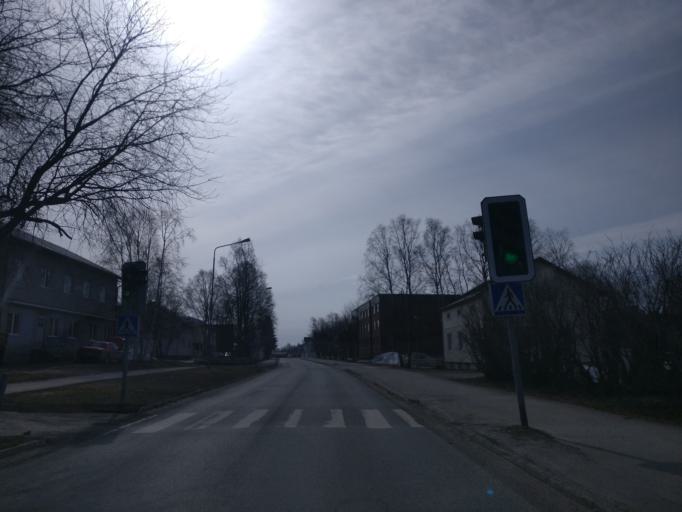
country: FI
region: Lapland
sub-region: Kemi-Tornio
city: Kemi
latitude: 65.7466
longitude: 24.5635
